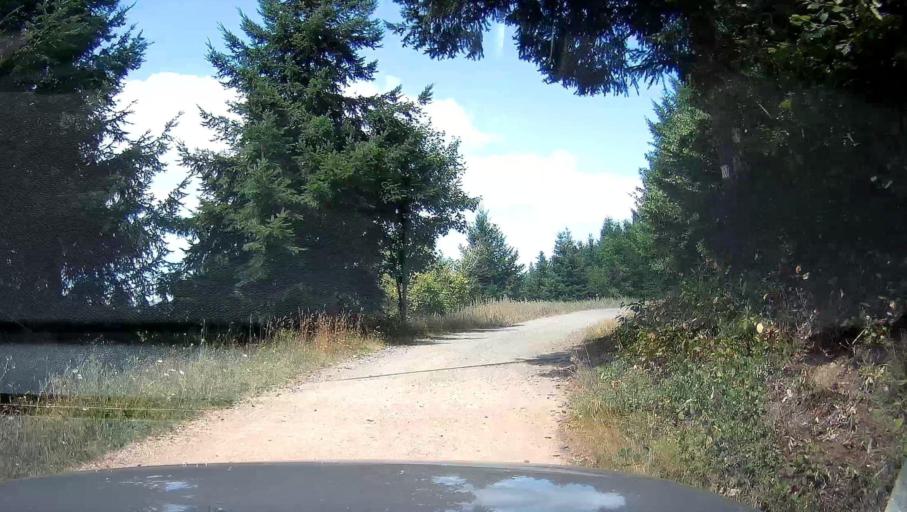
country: FR
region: Rhone-Alpes
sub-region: Departement du Rhone
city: Grandris
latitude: 46.0179
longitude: 4.5396
